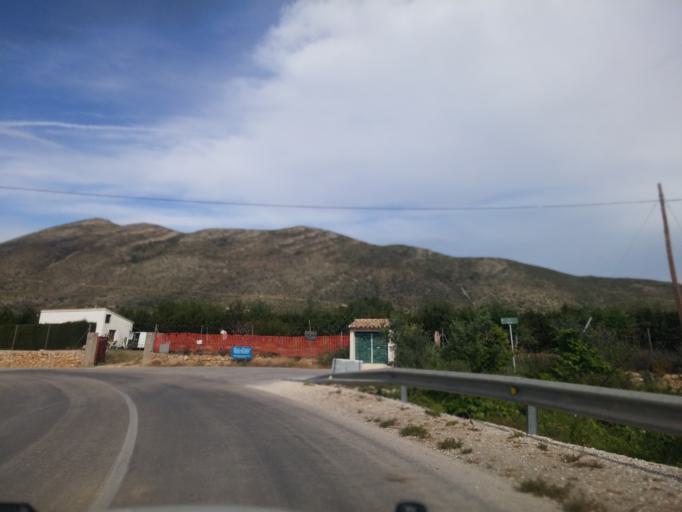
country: ES
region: Valencia
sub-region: Provincia de Alicante
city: Benissa
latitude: 38.7070
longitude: 0.0254
